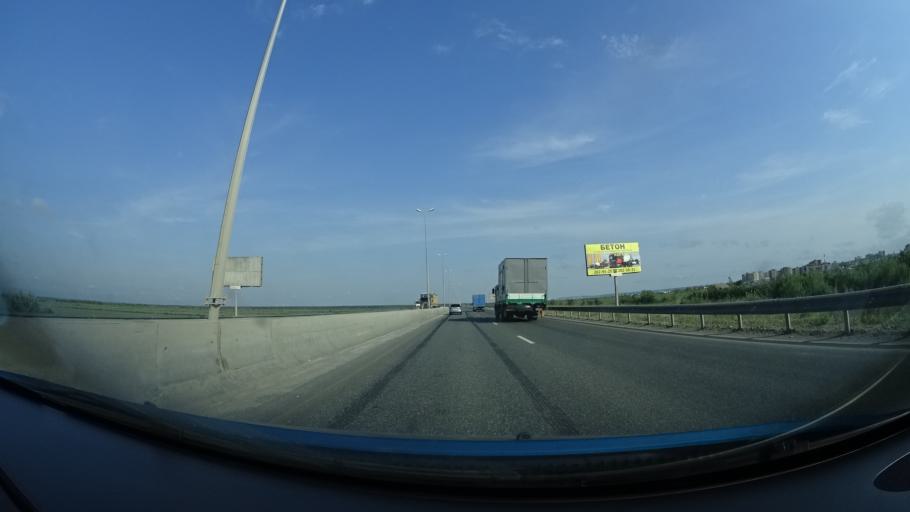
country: RU
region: Perm
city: Kondratovo
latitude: 57.9666
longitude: 56.0997
